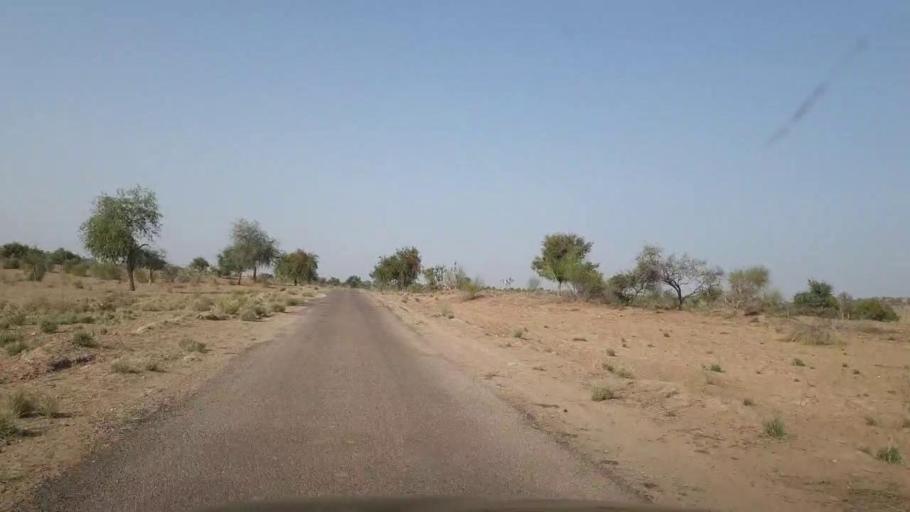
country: PK
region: Sindh
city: Islamkot
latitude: 25.1349
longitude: 70.5177
